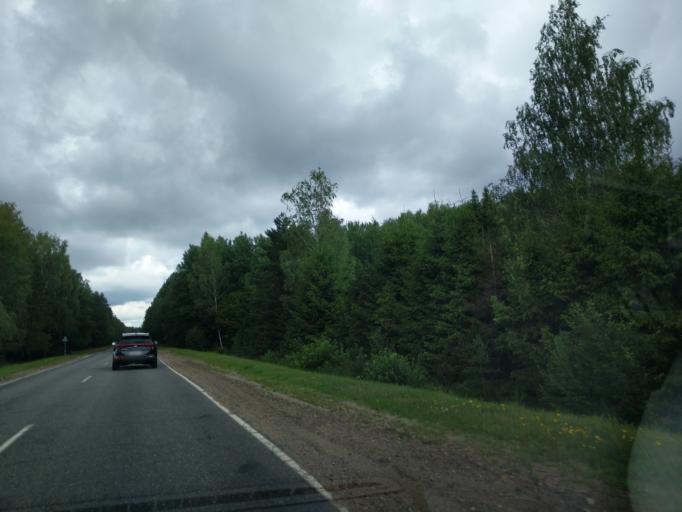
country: BY
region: Minsk
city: Il'ya
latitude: 54.4814
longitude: 27.2476
